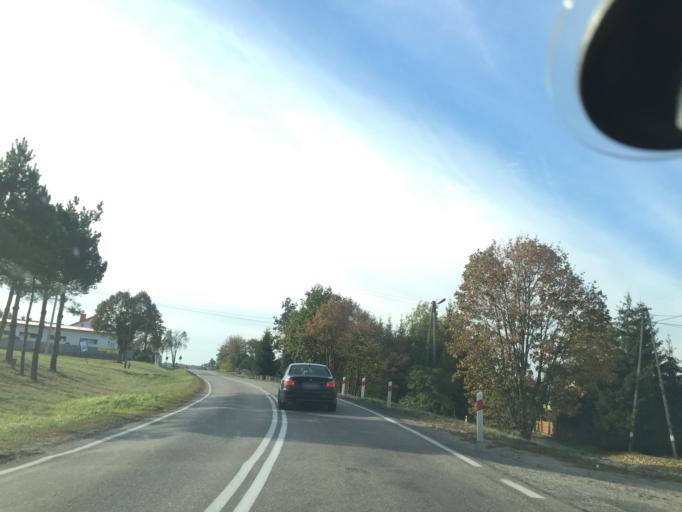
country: PL
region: Warmian-Masurian Voivodeship
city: Dobre Miasto
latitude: 54.0288
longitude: 20.4105
